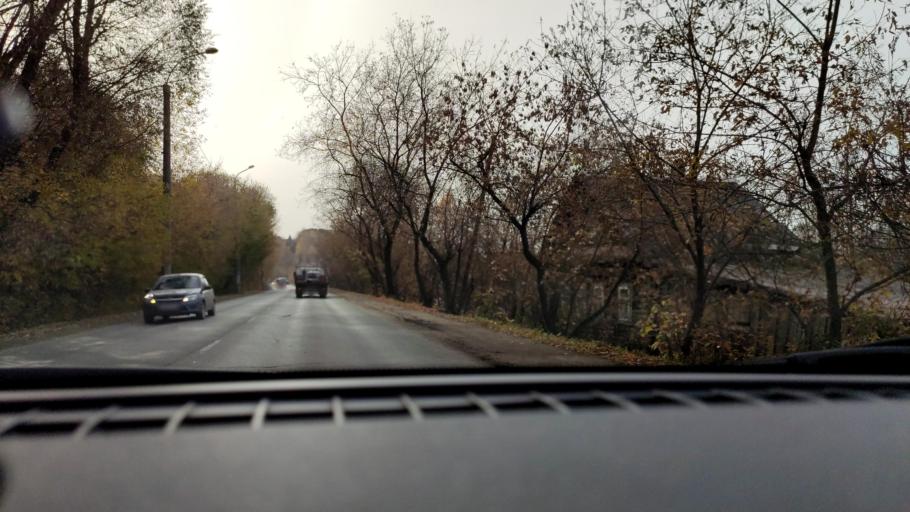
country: RU
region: Perm
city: Perm
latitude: 58.0607
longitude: 56.3388
